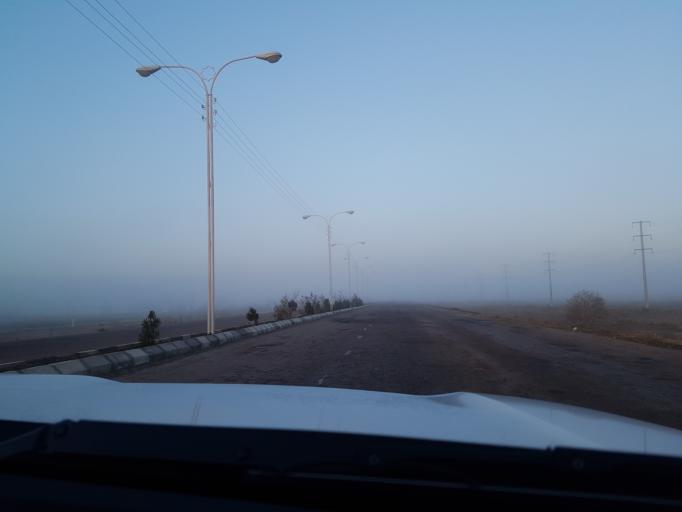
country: TM
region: Dasoguz
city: Koeneuergench
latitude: 41.7427
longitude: 58.7048
